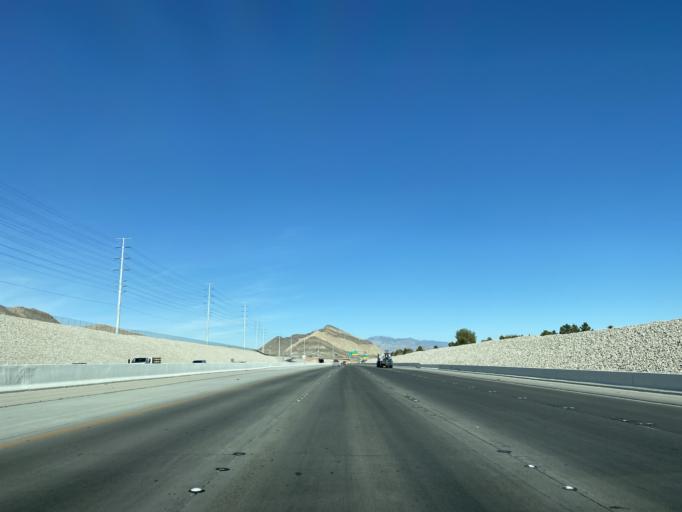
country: US
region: Nevada
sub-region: Clark County
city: Summerlin South
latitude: 36.1972
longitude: -115.3417
